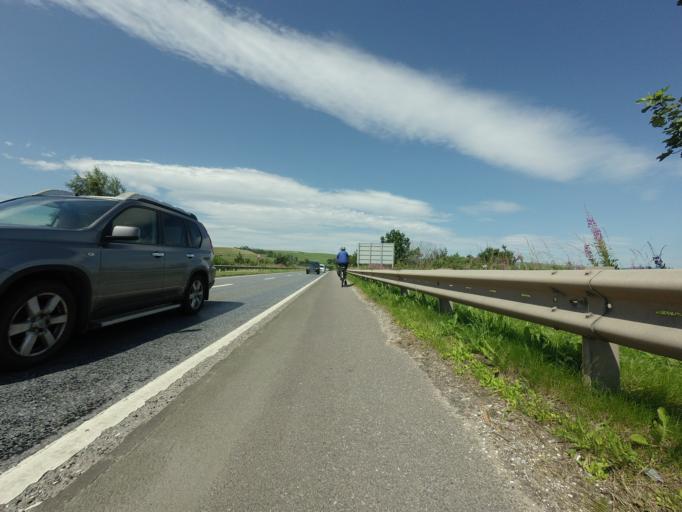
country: GB
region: Scotland
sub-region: Highland
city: Conon Bridge
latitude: 57.5744
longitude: -4.4314
